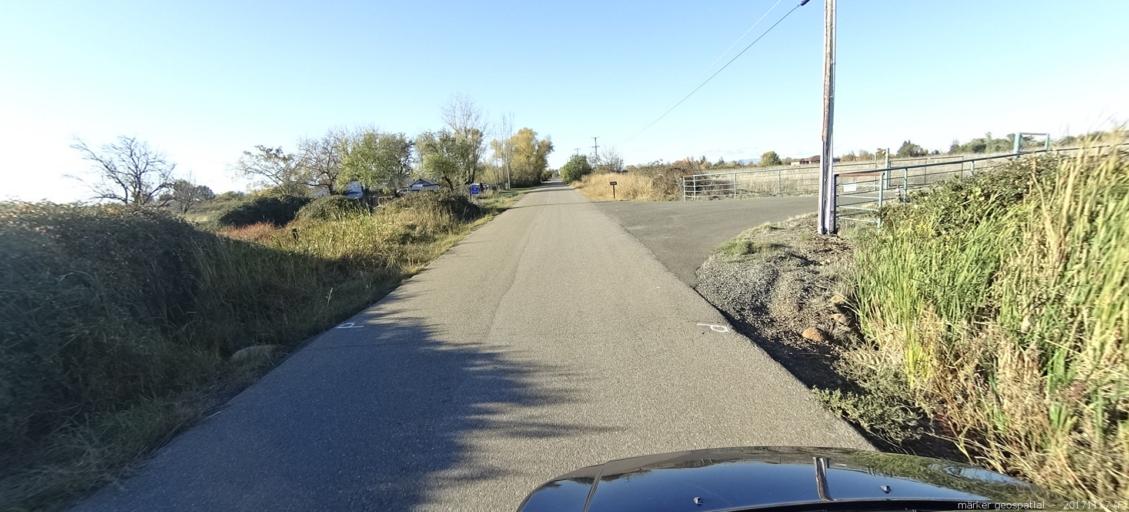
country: US
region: California
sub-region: Shasta County
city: Cottonwood
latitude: 40.4178
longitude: -122.2275
